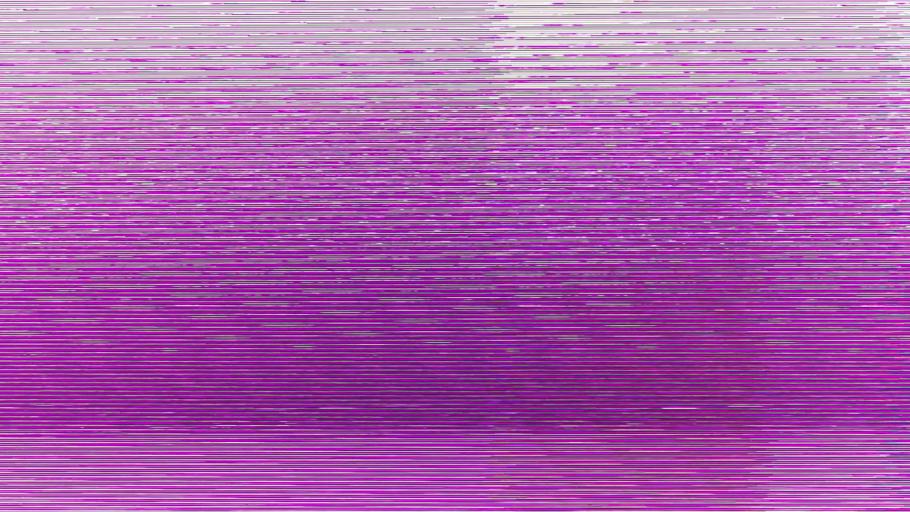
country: US
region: Michigan
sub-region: Livingston County
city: Whitmore Lake
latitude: 42.4678
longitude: -83.7966
